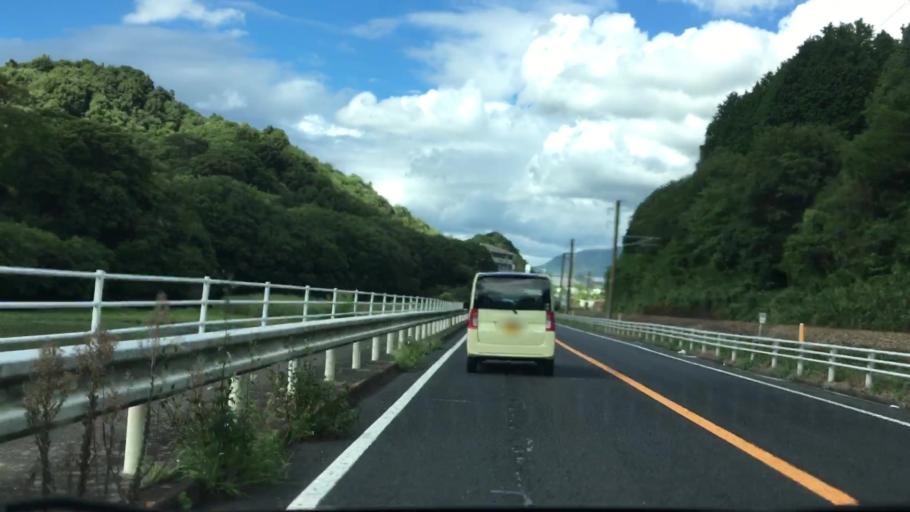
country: JP
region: Saga Prefecture
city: Imaricho-ko
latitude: 33.1721
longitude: 129.8448
